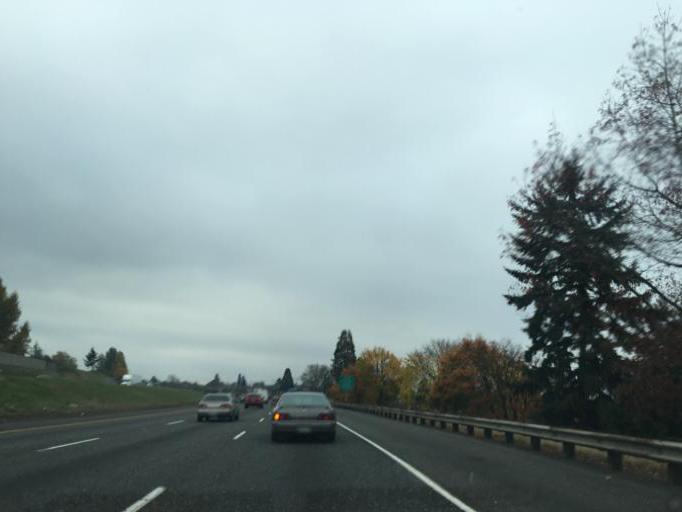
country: US
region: Oregon
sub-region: Multnomah County
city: Lents
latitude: 45.4619
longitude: -122.5710
